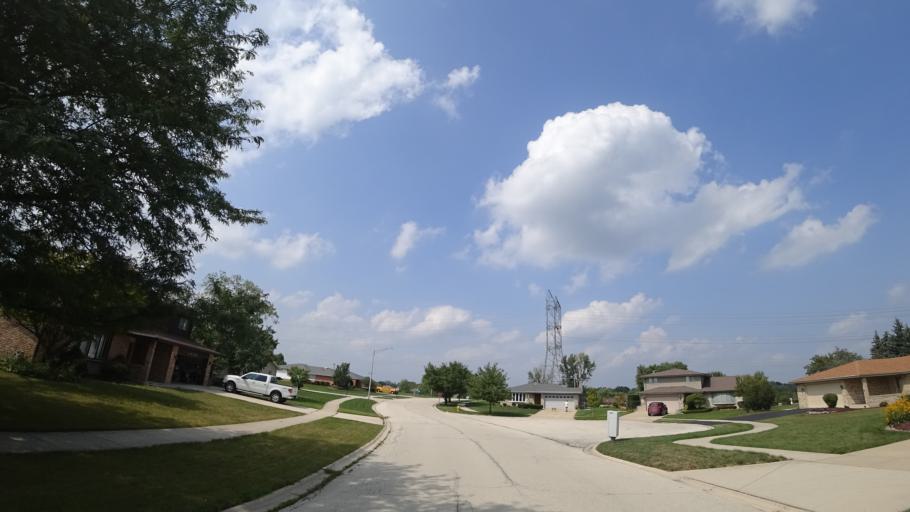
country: US
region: Illinois
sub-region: Will County
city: Goodings Grove
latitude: 41.6397
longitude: -87.9030
